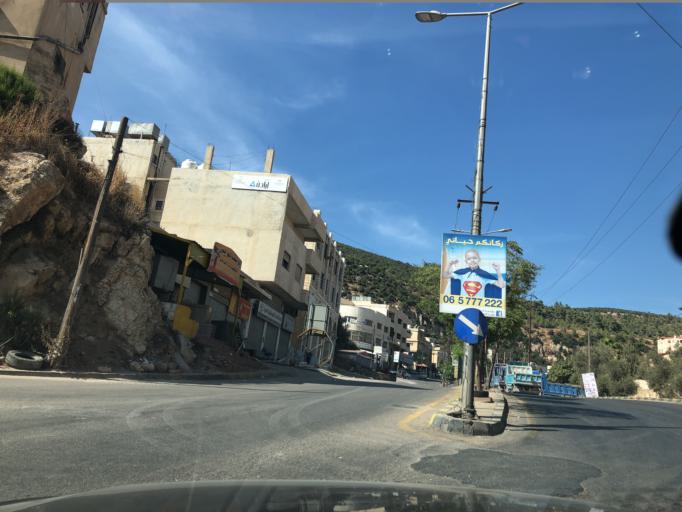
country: JO
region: Ajlun
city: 'Ajlun
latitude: 32.3344
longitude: 35.7519
